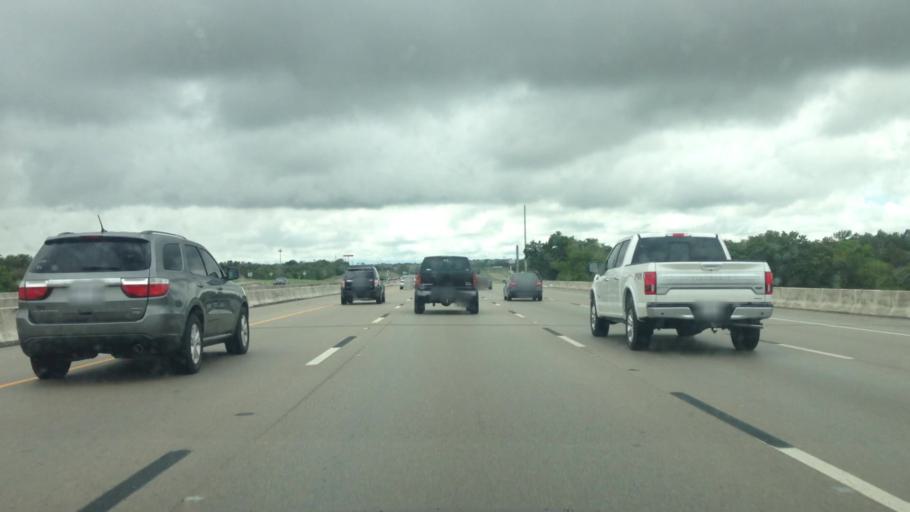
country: US
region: Texas
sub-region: Tarrant County
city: Lake Worth
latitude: 32.7908
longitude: -97.4570
